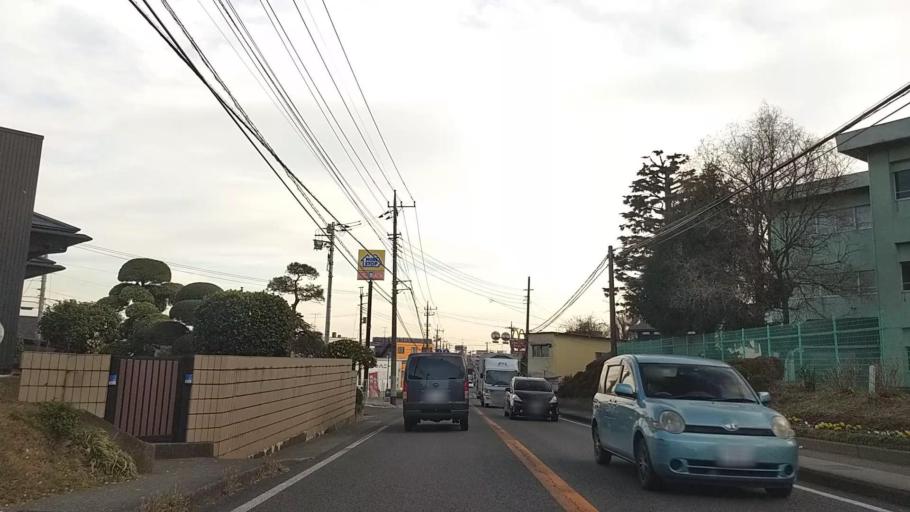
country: JP
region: Kanagawa
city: Atsugi
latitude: 35.4662
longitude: 139.3539
